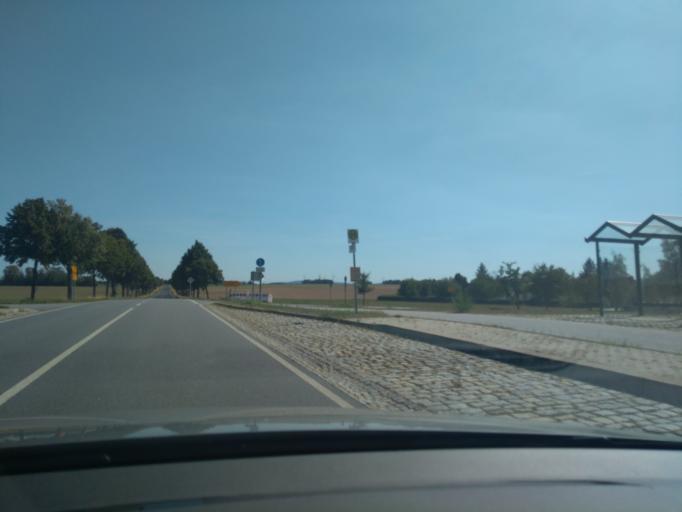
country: DE
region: Saxony
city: Panschwitz-Kuckau
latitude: 51.2278
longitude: 14.2140
